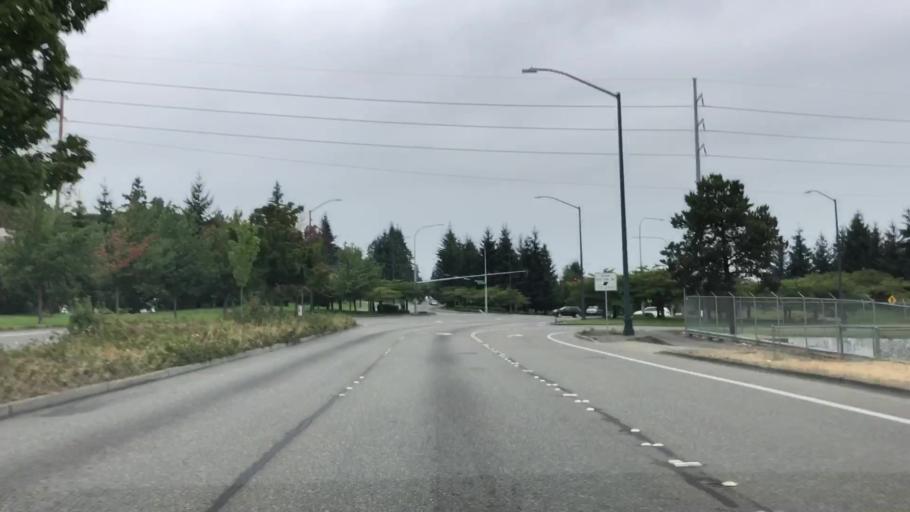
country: US
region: Washington
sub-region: Kitsap County
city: Navy Yard City
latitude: 47.5581
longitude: -122.6555
